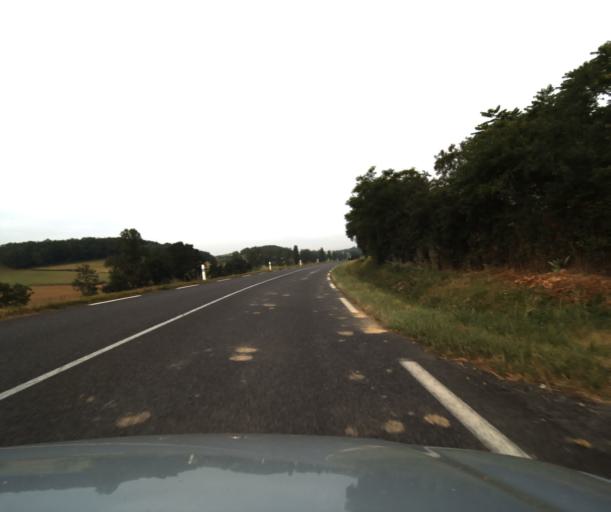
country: FR
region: Midi-Pyrenees
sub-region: Departement du Gers
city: Pavie
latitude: 43.5634
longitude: 0.5152
